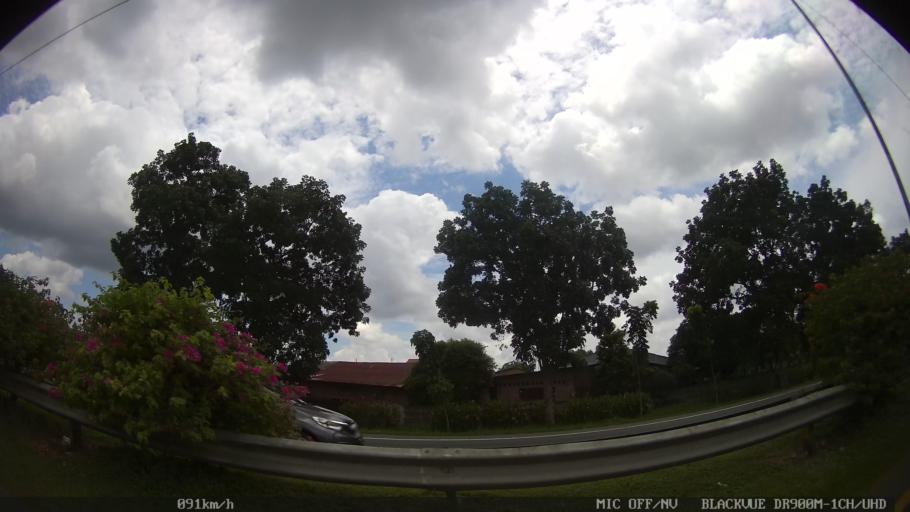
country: ID
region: North Sumatra
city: Medan
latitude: 3.6185
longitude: 98.7206
